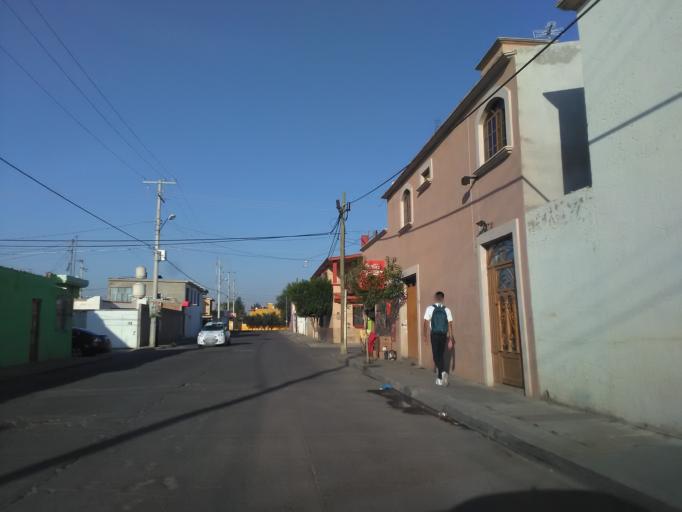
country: MX
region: Durango
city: Victoria de Durango
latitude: 24.0568
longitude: -104.6218
